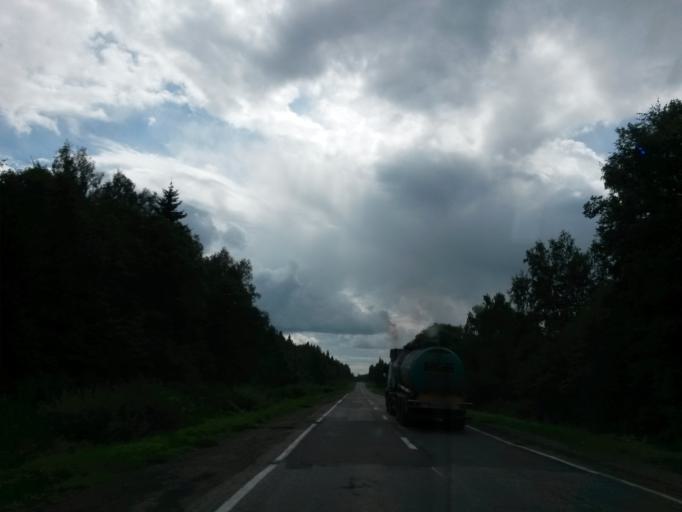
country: RU
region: Jaroslavl
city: Yaroslavl
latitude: 57.4992
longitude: 39.8997
